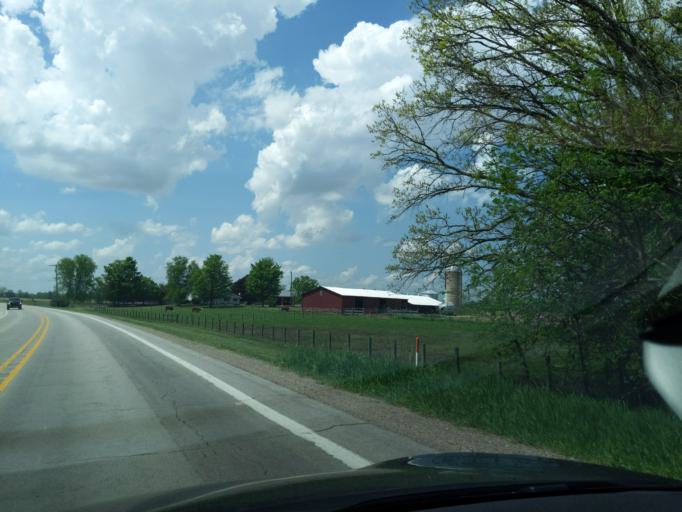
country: US
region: Michigan
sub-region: Ingham County
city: Stockbridge
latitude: 42.5550
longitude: -84.2360
